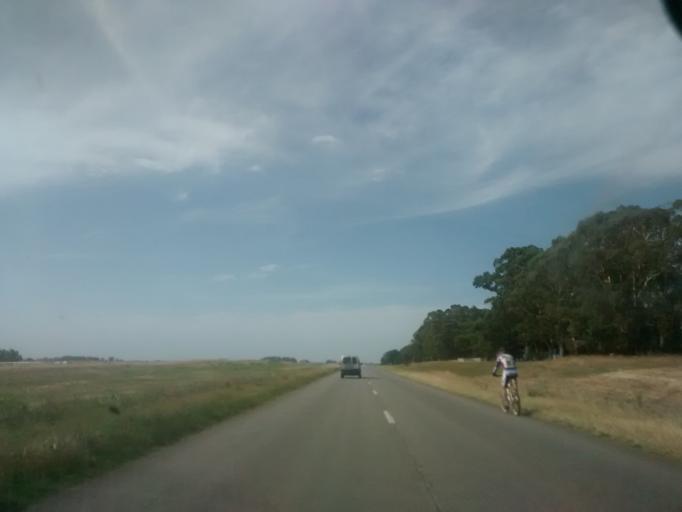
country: AR
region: Buenos Aires
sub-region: Partido de Loberia
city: Loberia
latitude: -37.8939
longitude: -58.6930
